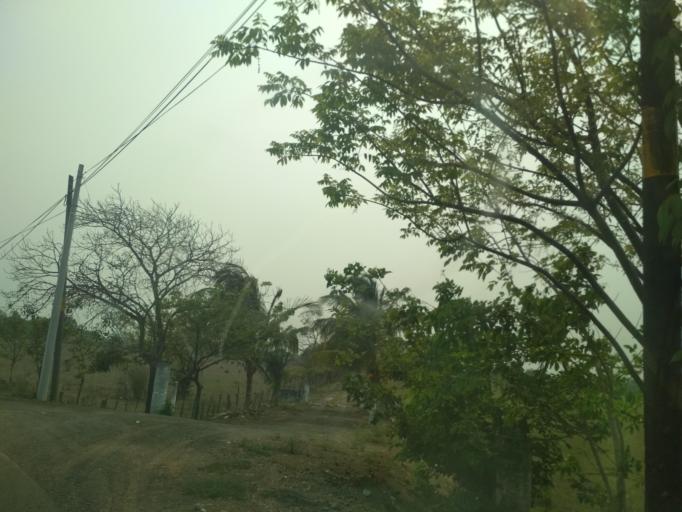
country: MX
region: Veracruz
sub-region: Veracruz
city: Delfino Victoria (Santa Fe)
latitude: 19.2093
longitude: -96.3191
